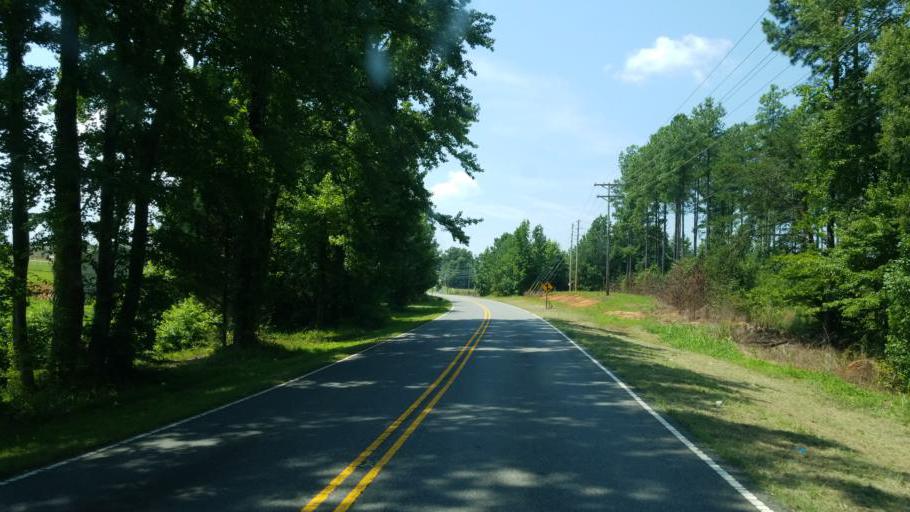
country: US
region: North Carolina
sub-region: Gaston County
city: Tryon
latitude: 35.3237
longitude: -81.3637
